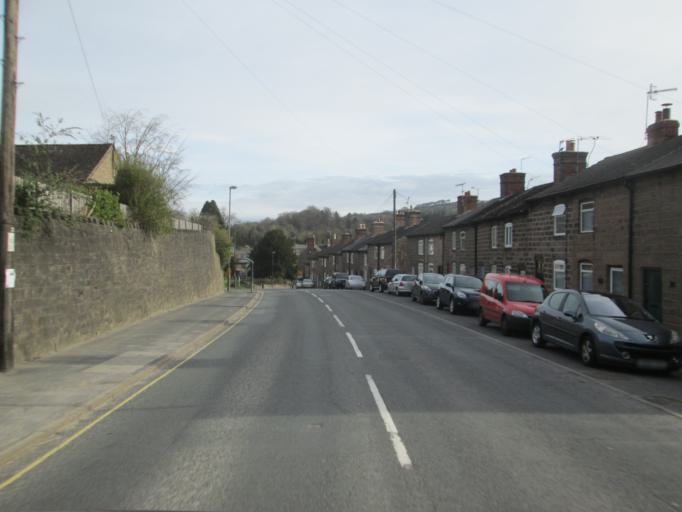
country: GB
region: England
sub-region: Derbyshire
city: Cromford
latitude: 53.1063
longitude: -1.5628
